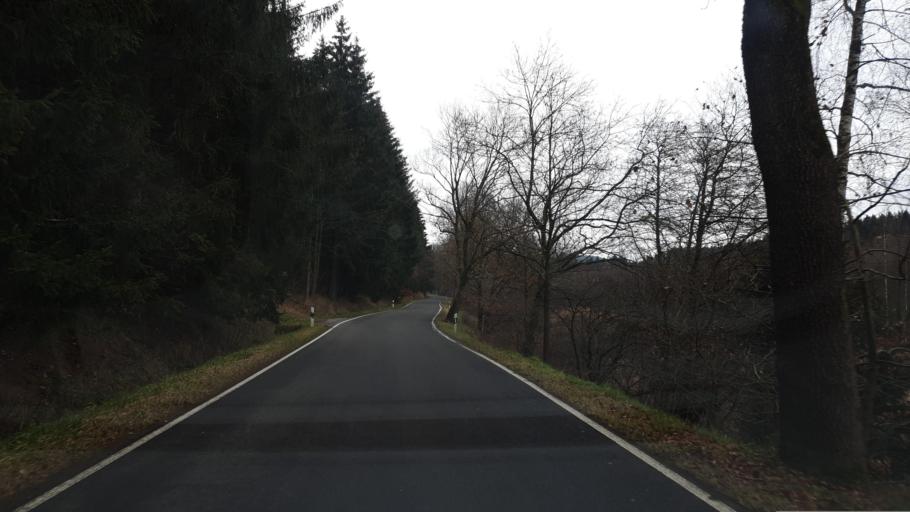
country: DE
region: Saxony
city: Mulda
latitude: 50.7866
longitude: 13.4115
